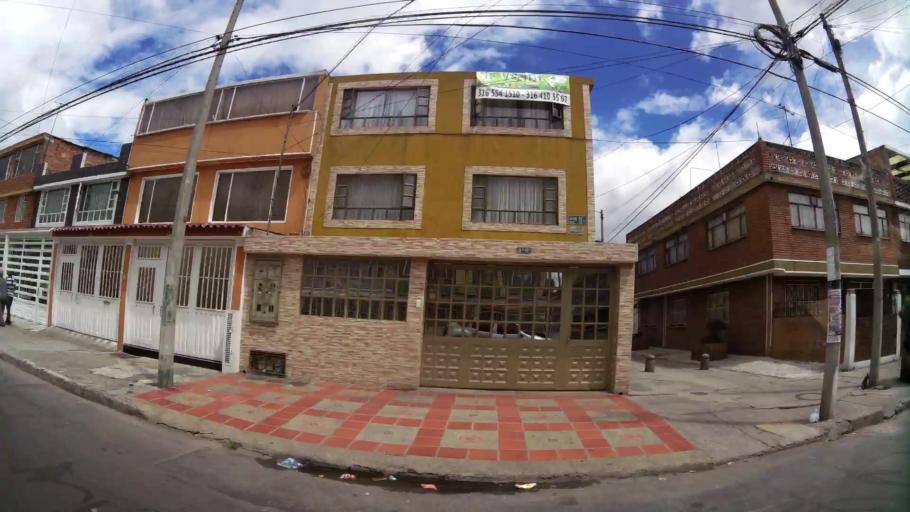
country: CO
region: Bogota D.C.
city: Bogota
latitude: 4.5990
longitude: -74.1218
